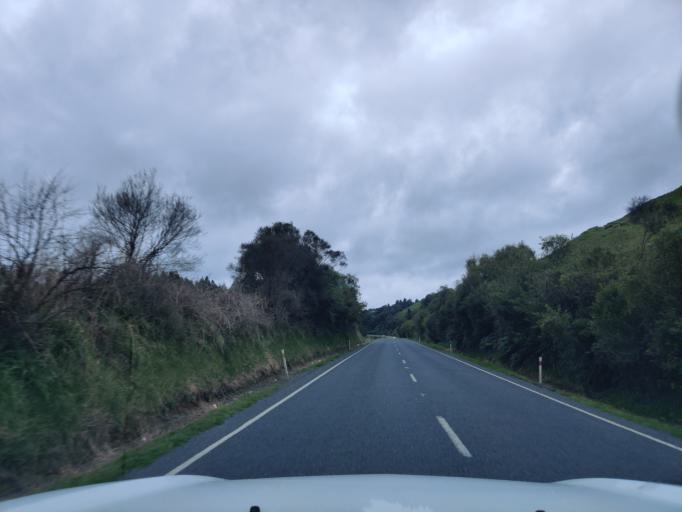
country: NZ
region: Waikato
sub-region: Otorohanga District
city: Otorohanga
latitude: -38.5486
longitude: 175.1863
